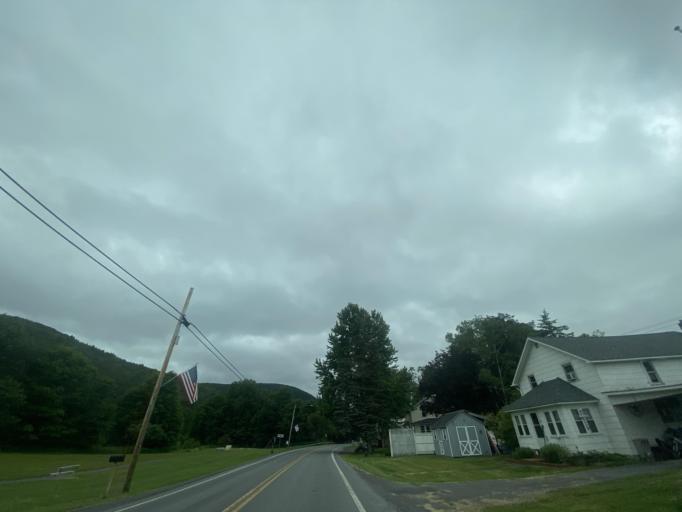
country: US
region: New York
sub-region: Schoharie County
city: Middleburgh
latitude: 42.3846
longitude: -74.3799
